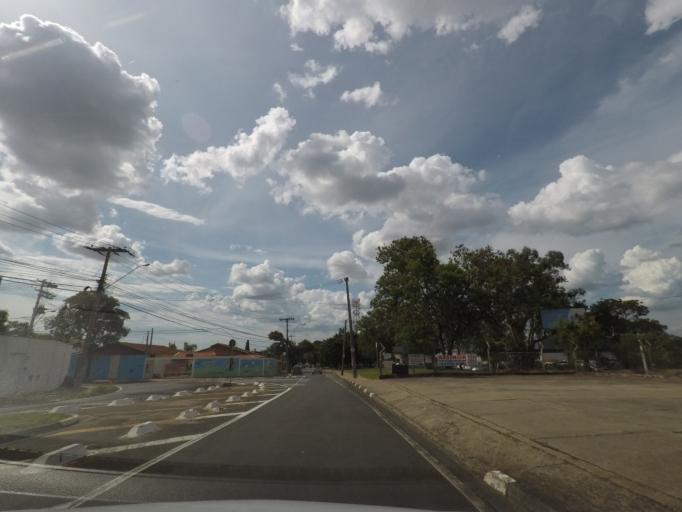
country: BR
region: Sao Paulo
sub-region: Campinas
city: Campinas
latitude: -22.8911
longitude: -47.1017
